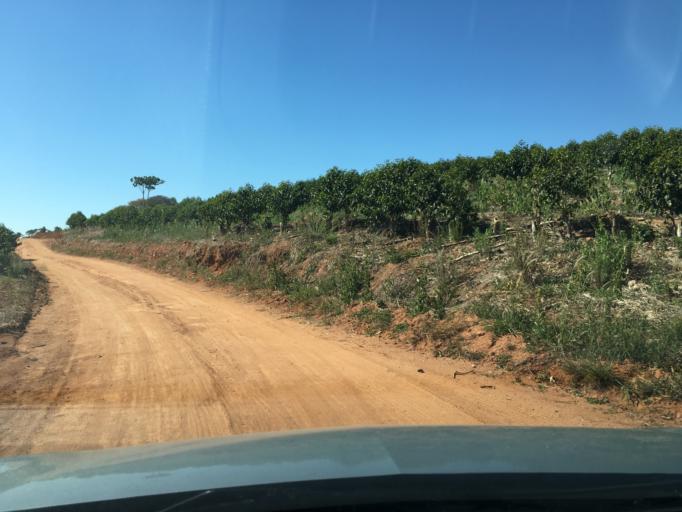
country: BR
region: Minas Gerais
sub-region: Campestre
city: Campestre
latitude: -21.5900
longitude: -46.2082
